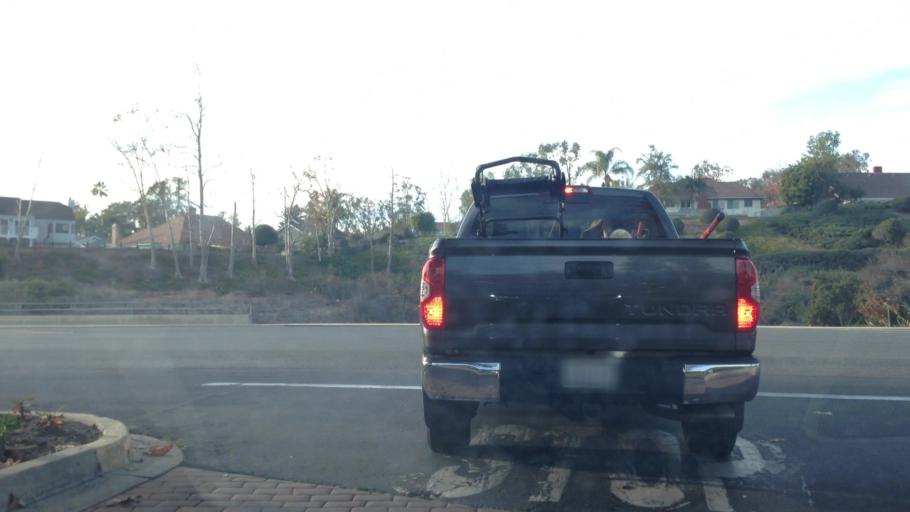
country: US
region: California
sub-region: Orange County
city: Lake Forest
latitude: 33.6445
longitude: -117.6652
